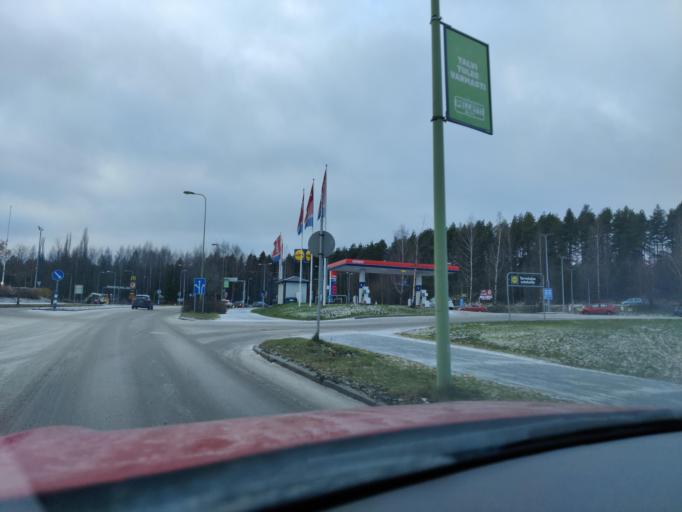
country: FI
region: Pirkanmaa
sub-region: Tampere
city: Nokia
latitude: 61.4663
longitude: 23.5068
